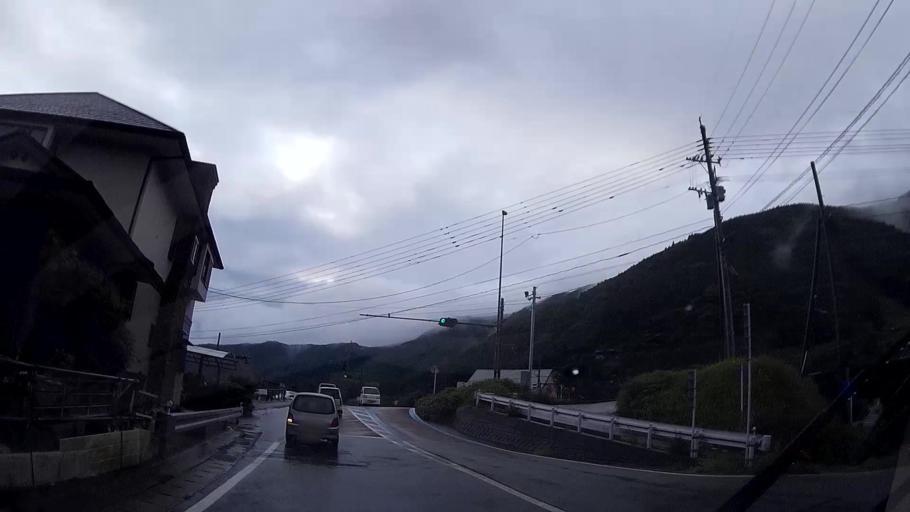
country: JP
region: Kumamoto
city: Ozu
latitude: 32.8777
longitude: 130.9756
